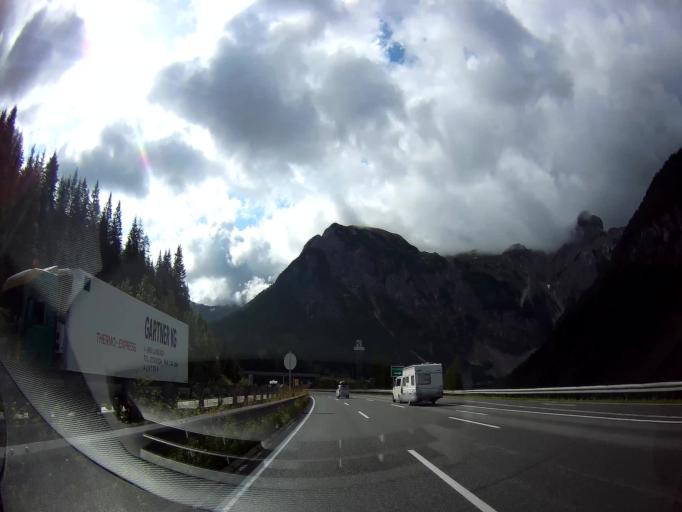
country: AT
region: Salzburg
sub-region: Politischer Bezirk Sankt Johann im Pongau
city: Untertauern
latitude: 47.2527
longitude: 13.4223
